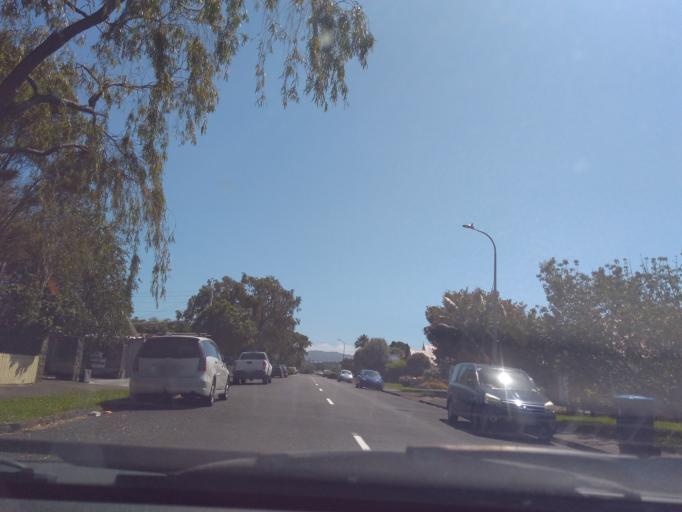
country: NZ
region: Auckland
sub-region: Auckland
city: Rosebank
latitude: -36.9001
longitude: 174.6920
